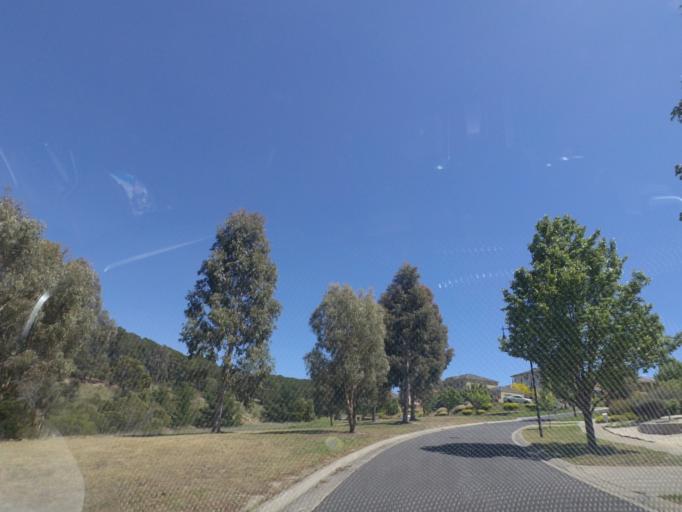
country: AU
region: Victoria
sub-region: Hume
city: Sunbury
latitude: -37.5570
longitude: 144.7067
